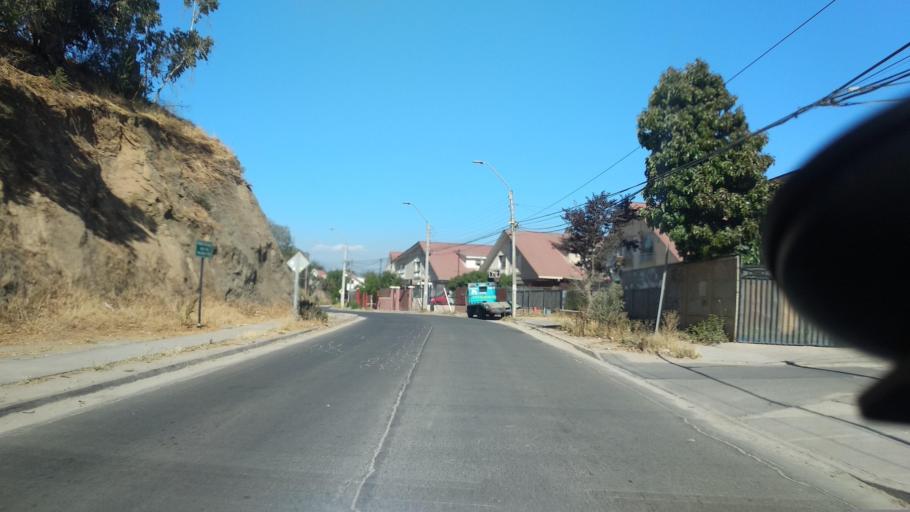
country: CL
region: Valparaiso
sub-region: Provincia de Marga Marga
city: Villa Alemana
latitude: -33.0388
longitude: -71.3901
